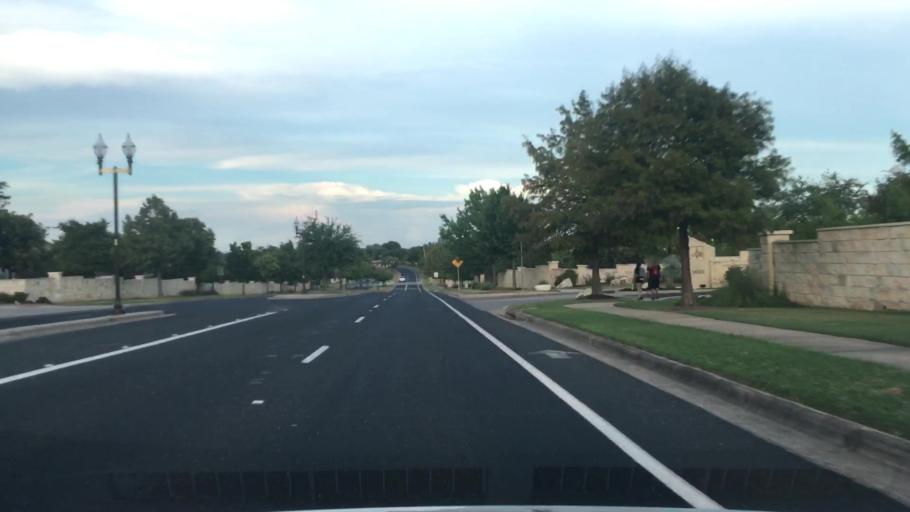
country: US
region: Texas
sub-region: Williamson County
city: Cedar Park
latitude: 30.4944
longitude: -97.7898
